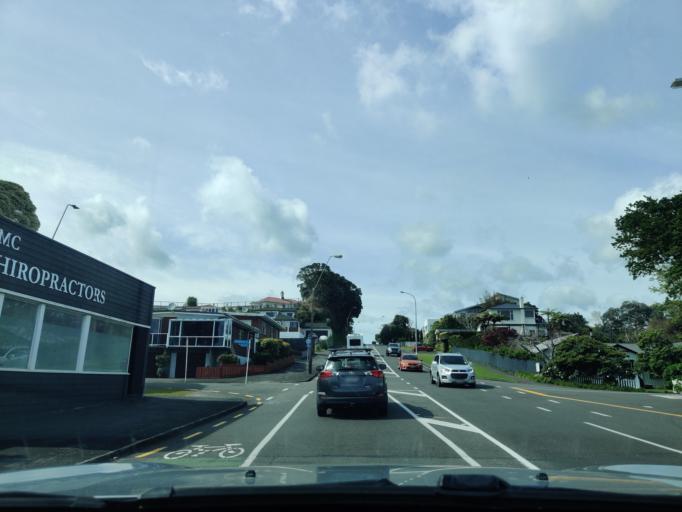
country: NZ
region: Taranaki
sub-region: New Plymouth District
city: New Plymouth
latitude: -39.0583
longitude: 174.0843
